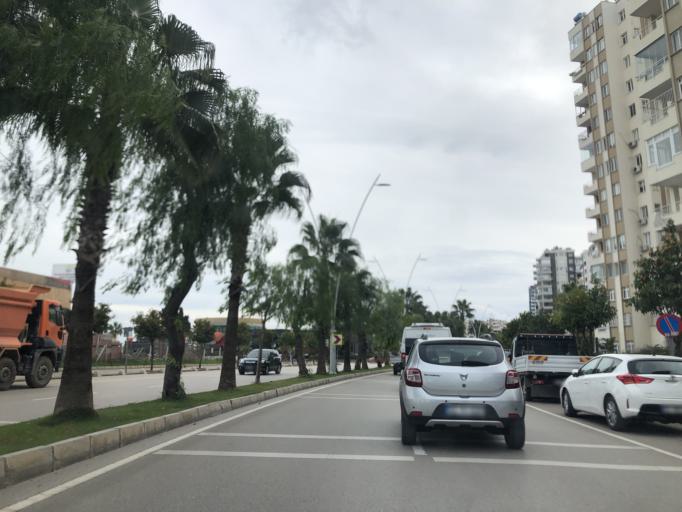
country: TR
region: Adana
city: Adana
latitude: 37.0567
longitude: 35.2863
